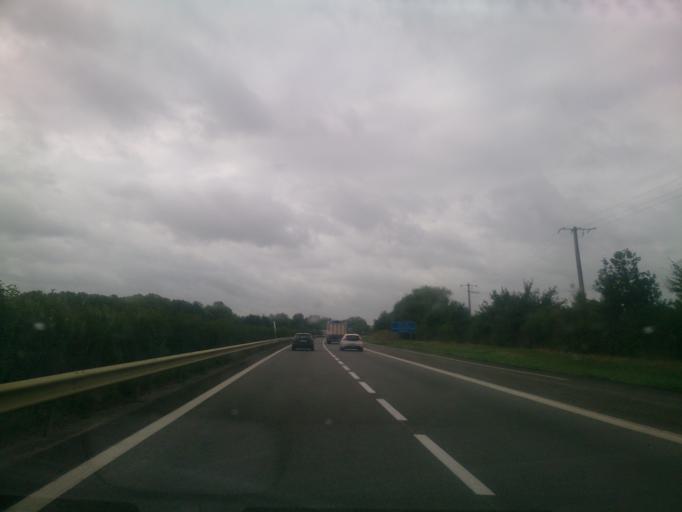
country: FR
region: Midi-Pyrenees
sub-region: Departement de la Haute-Garonne
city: Noe
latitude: 43.3530
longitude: 1.2680
